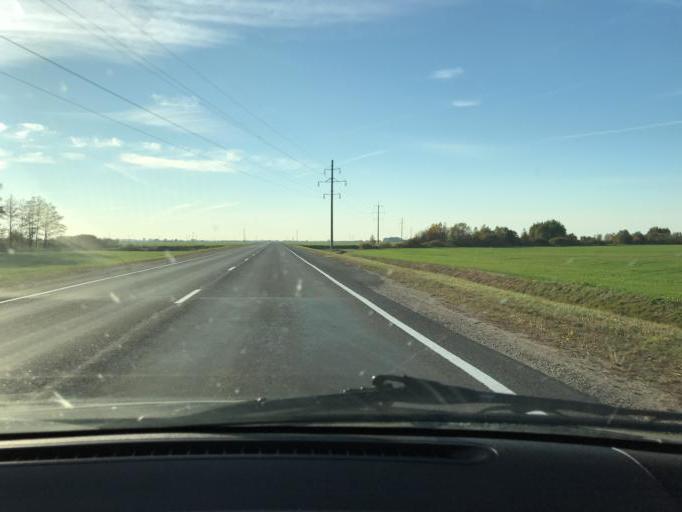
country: BY
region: Brest
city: Antopal'
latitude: 52.2262
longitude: 24.7545
